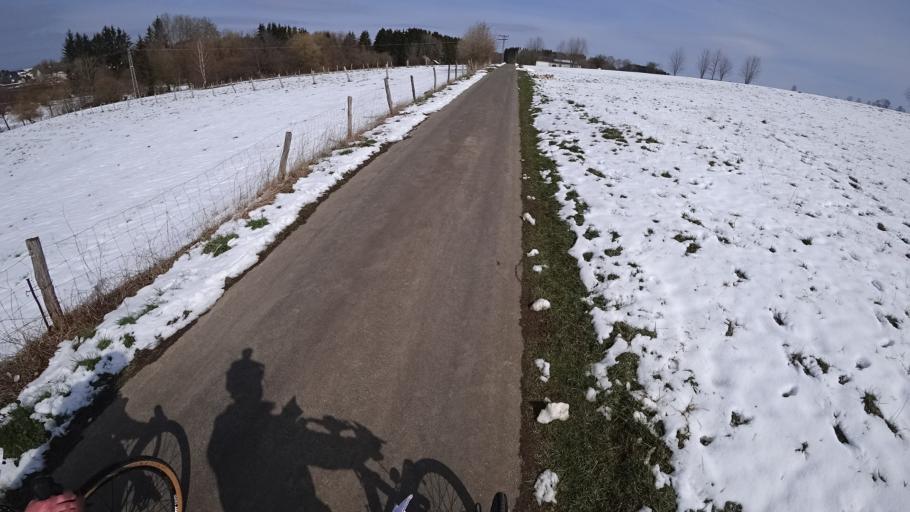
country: DE
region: Rheinland-Pfalz
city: Morlen
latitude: 50.7000
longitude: 7.8840
